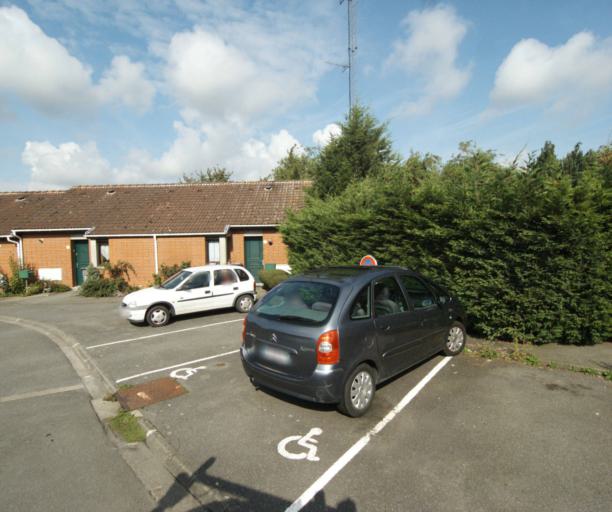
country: FR
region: Nord-Pas-de-Calais
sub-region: Departement du Nord
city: Perenchies
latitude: 50.6717
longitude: 2.9705
